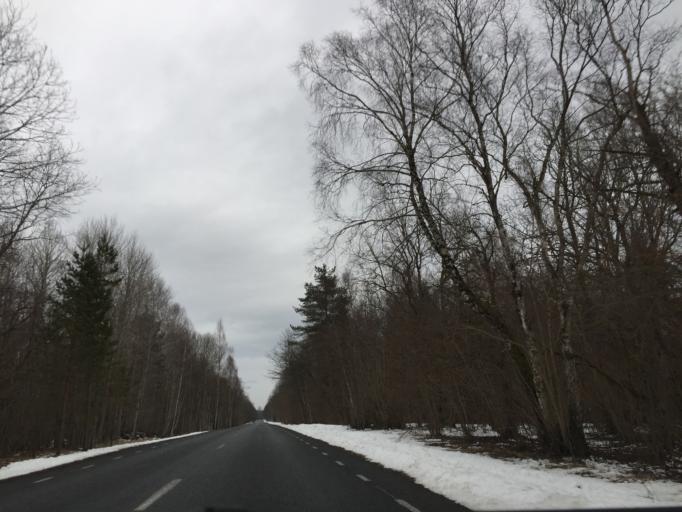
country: EE
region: Saare
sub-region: Orissaare vald
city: Orissaare
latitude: 58.5670
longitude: 22.7643
